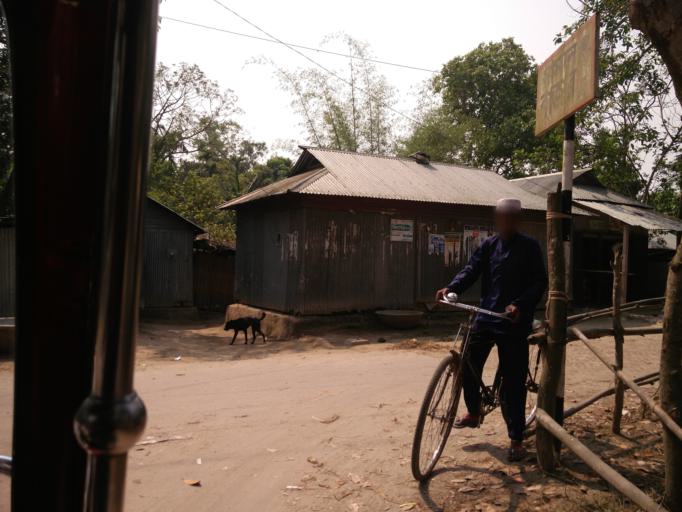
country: BD
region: Dhaka
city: Muktagacha
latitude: 24.8985
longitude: 90.2598
